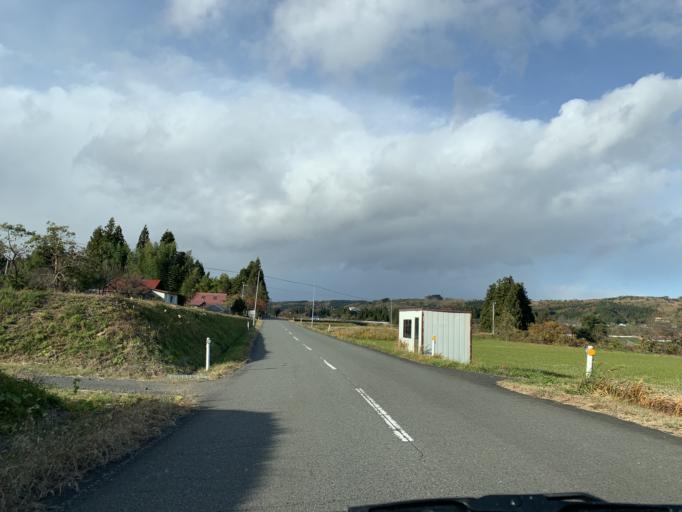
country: JP
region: Iwate
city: Ichinoseki
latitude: 39.0225
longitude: 141.0744
